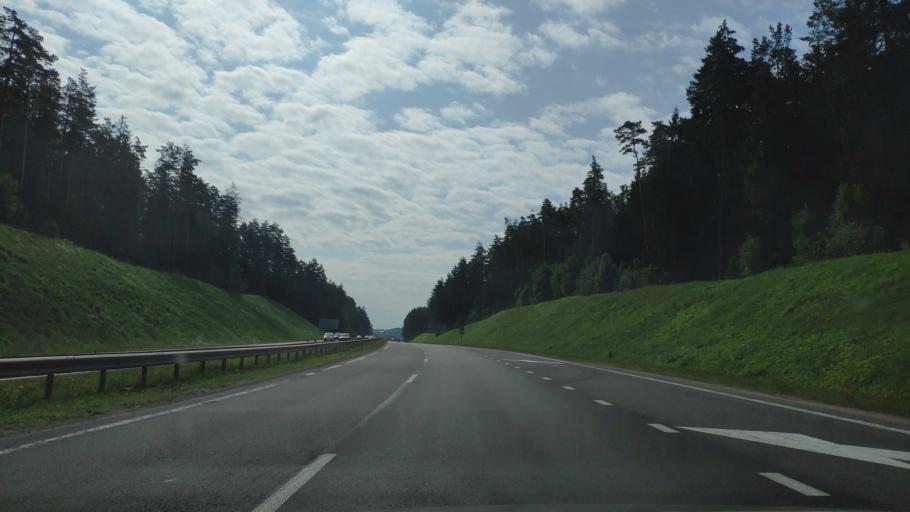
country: BY
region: Minsk
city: Khatsyezhyna
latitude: 53.9593
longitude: 27.3180
